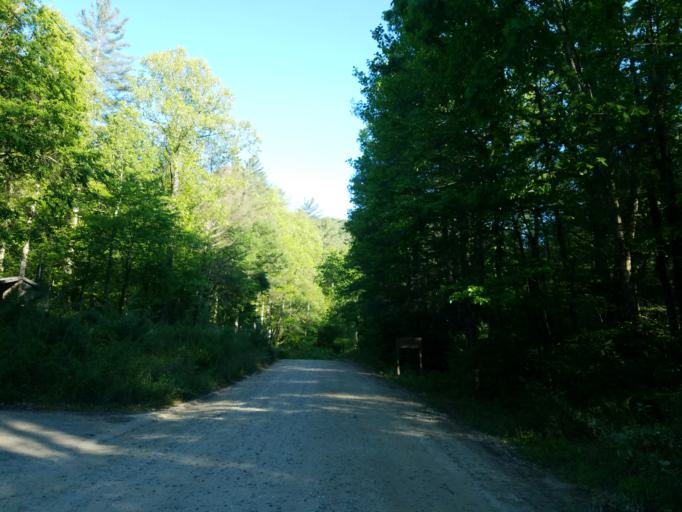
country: US
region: Georgia
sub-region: Fannin County
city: Blue Ridge
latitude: 34.7246
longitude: -84.1499
